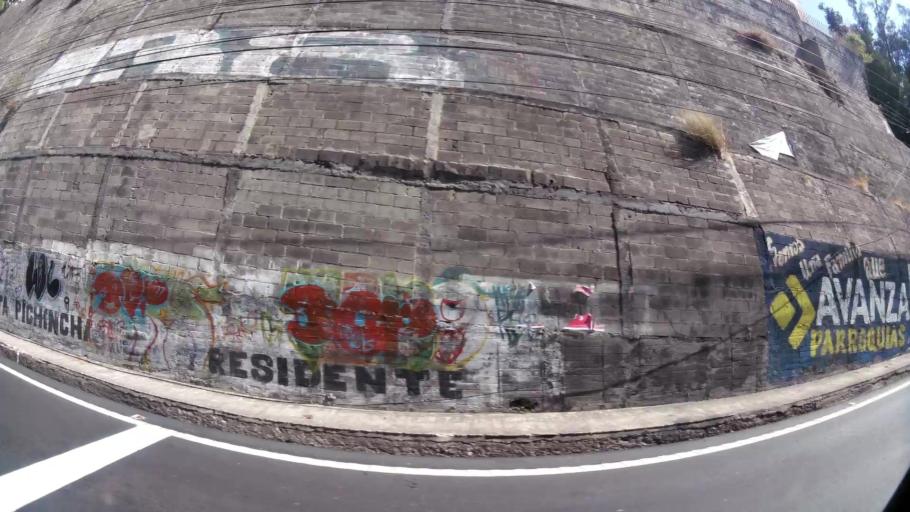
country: EC
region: Pichincha
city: Quito
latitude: -0.1907
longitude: -78.4424
